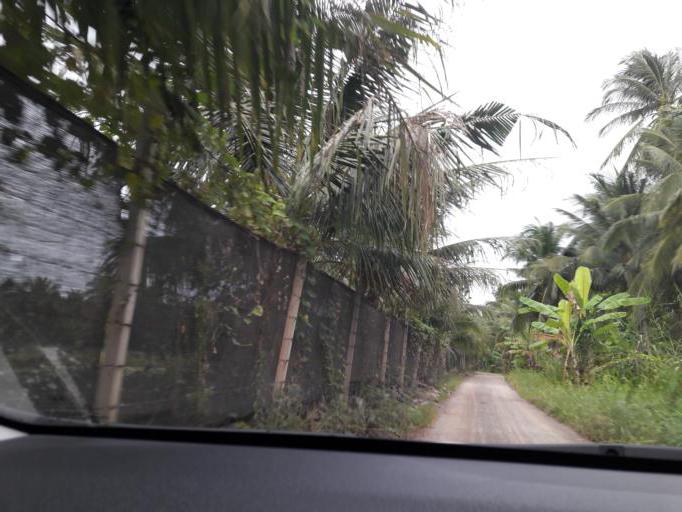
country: TH
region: Ratchaburi
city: Damnoen Saduak
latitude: 13.5374
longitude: 100.0371
